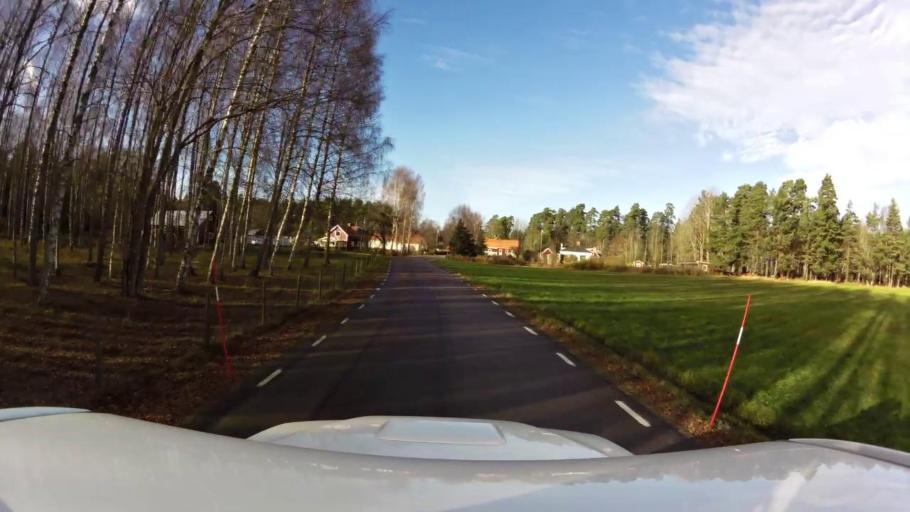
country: SE
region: OEstergoetland
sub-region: Linkopings Kommun
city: Linkoping
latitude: 58.3267
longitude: 15.6403
